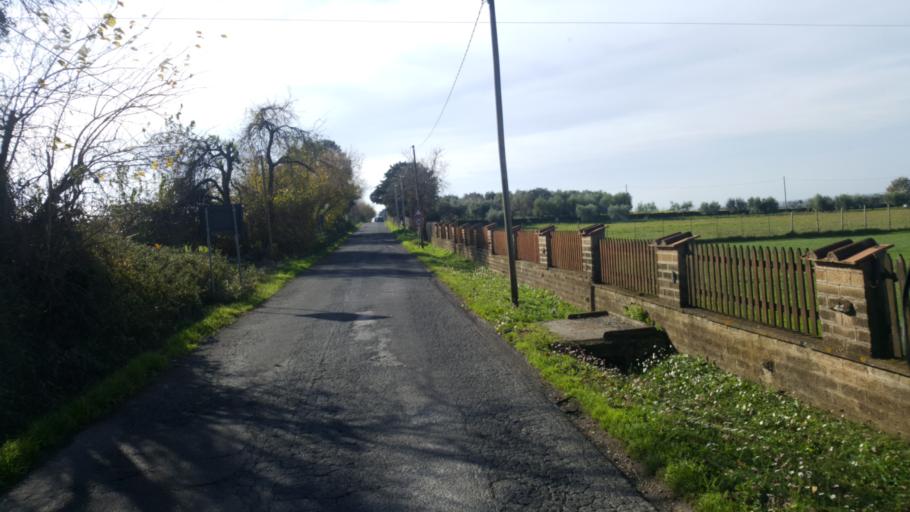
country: IT
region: Latium
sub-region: Citta metropolitana di Roma Capitale
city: Mantiglia di Ardea
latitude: 41.6695
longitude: 12.6361
